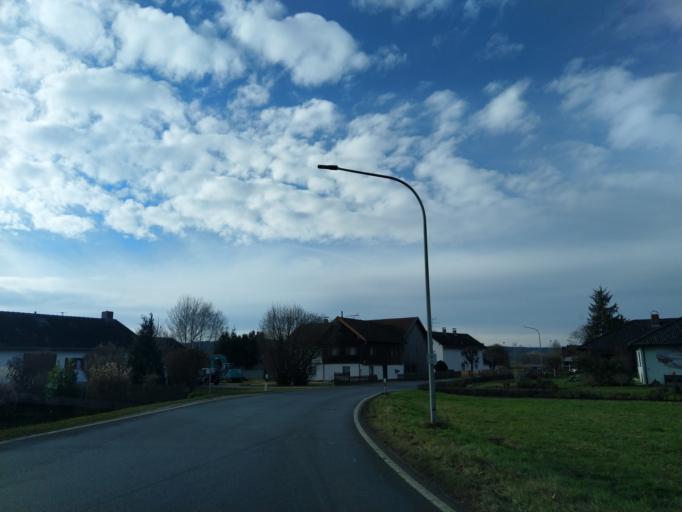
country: DE
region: Bavaria
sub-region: Lower Bavaria
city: Rossbach
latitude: 48.6220
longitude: 12.9602
